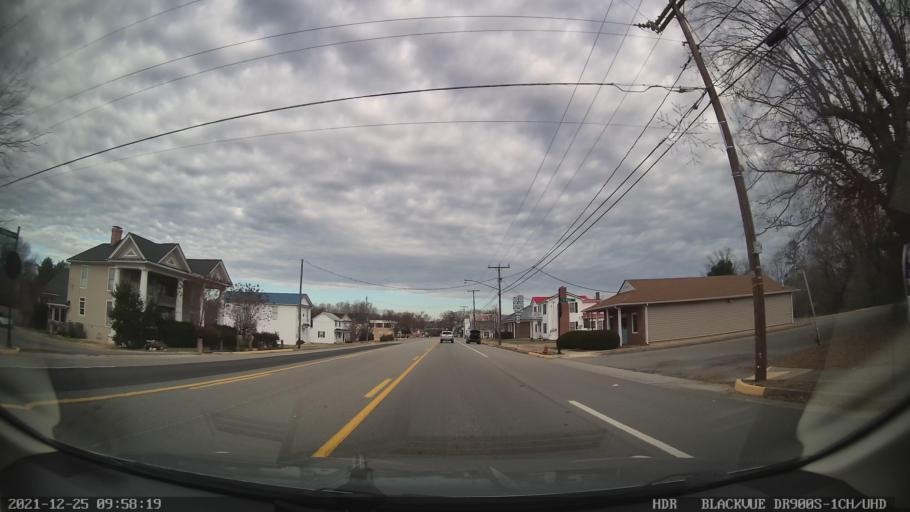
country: US
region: Virginia
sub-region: Louisa County
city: Louisa
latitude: 38.0080
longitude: -77.9088
